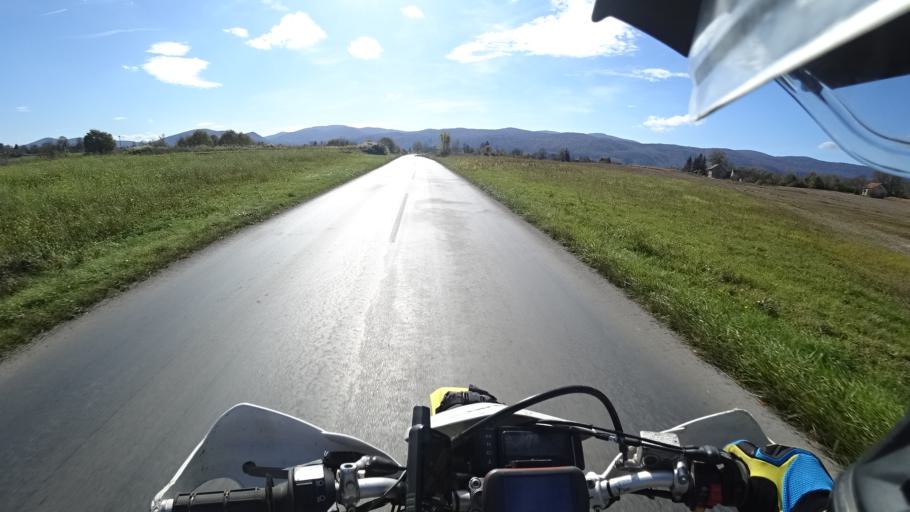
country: HR
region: Karlovacka
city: Plaski
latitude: 45.1063
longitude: 15.3595
